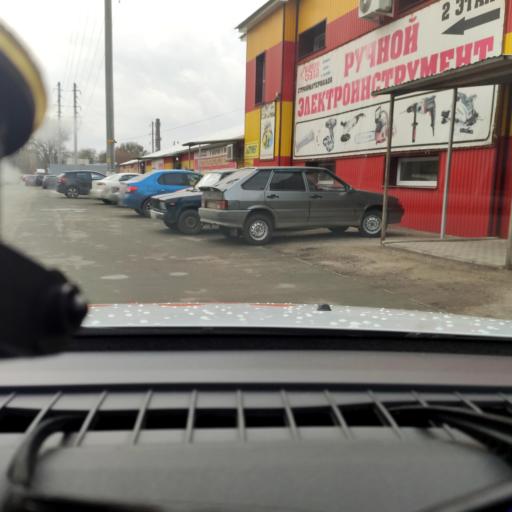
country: RU
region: Samara
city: Chapayevsk
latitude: 52.9736
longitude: 49.7133
